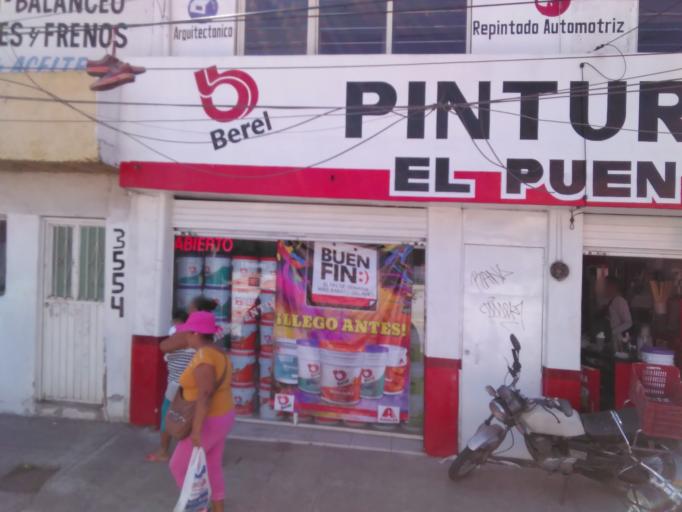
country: MX
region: Nayarit
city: Xalisco
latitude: 21.4744
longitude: -104.8603
